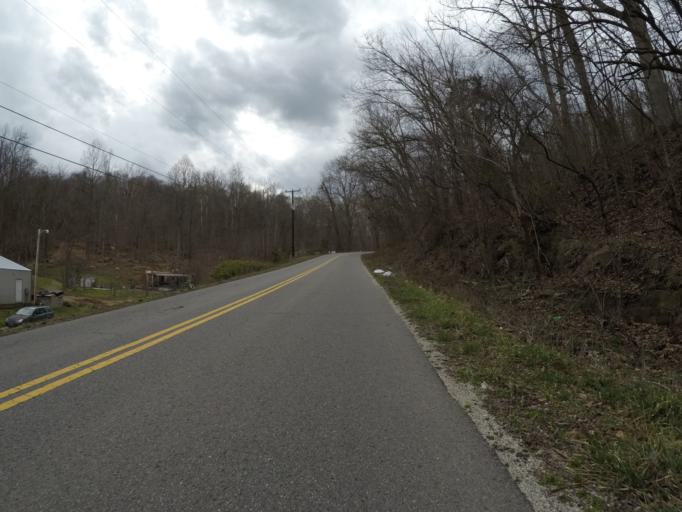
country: US
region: Ohio
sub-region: Lawrence County
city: Burlington
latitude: 38.4290
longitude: -82.5236
